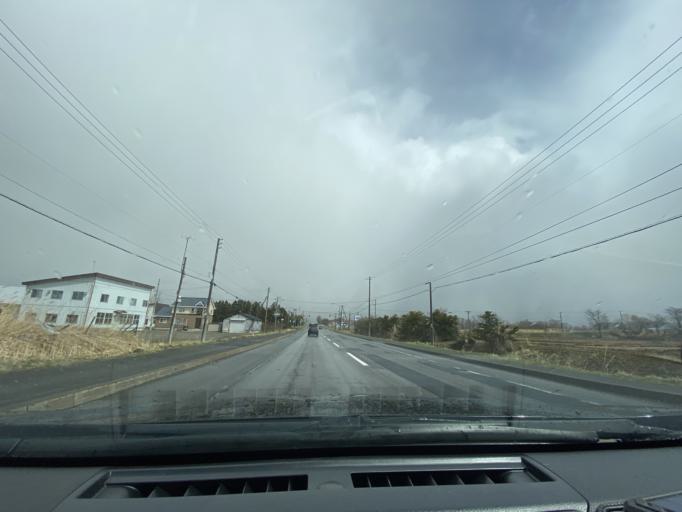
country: JP
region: Hokkaido
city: Takikawa
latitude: 43.6024
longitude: 141.9299
